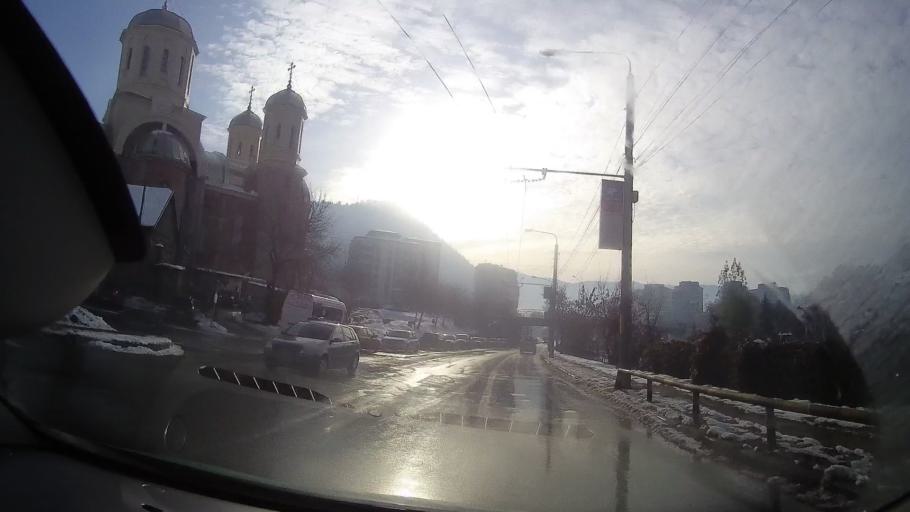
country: RO
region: Neamt
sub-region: Municipiul Piatra-Neamt
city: Valeni
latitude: 46.9374
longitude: 26.3804
